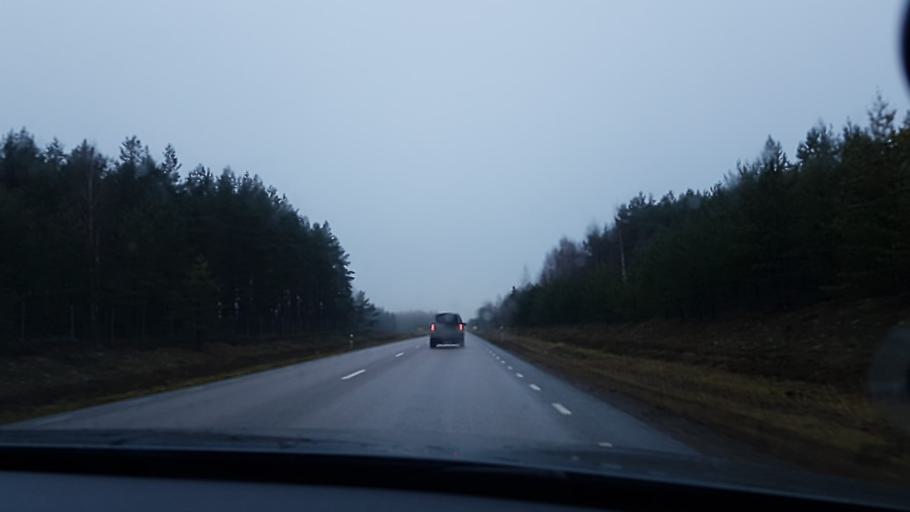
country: SE
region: Vaestra Goetaland
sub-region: Toreboda Kommun
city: Toereboda
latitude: 58.8117
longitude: 13.9795
